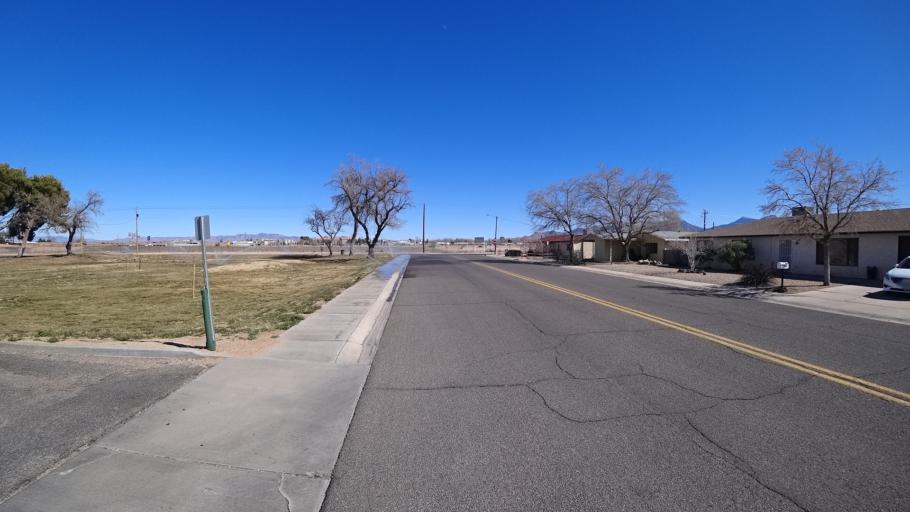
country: US
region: Arizona
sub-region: Mohave County
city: Kingman
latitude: 35.2141
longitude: -114.0299
